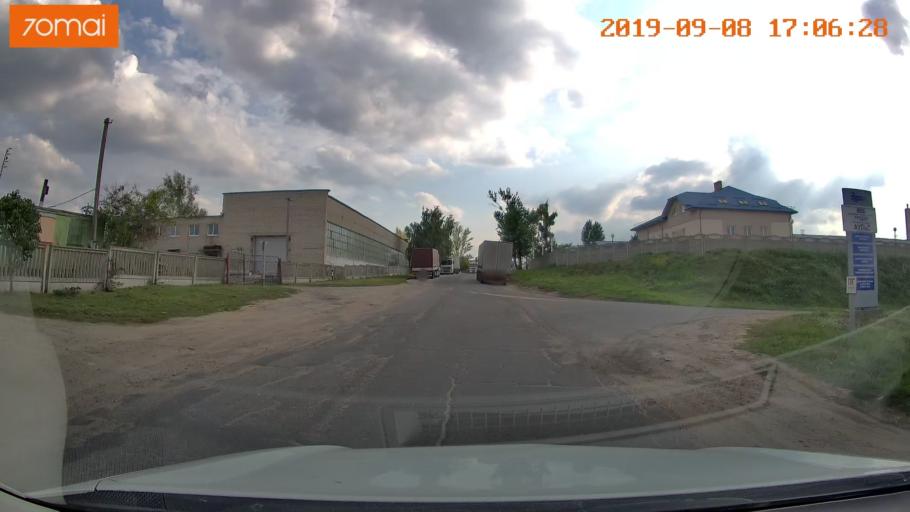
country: BY
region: Grodnenskaya
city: Hrodna
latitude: 53.6702
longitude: 23.9527
